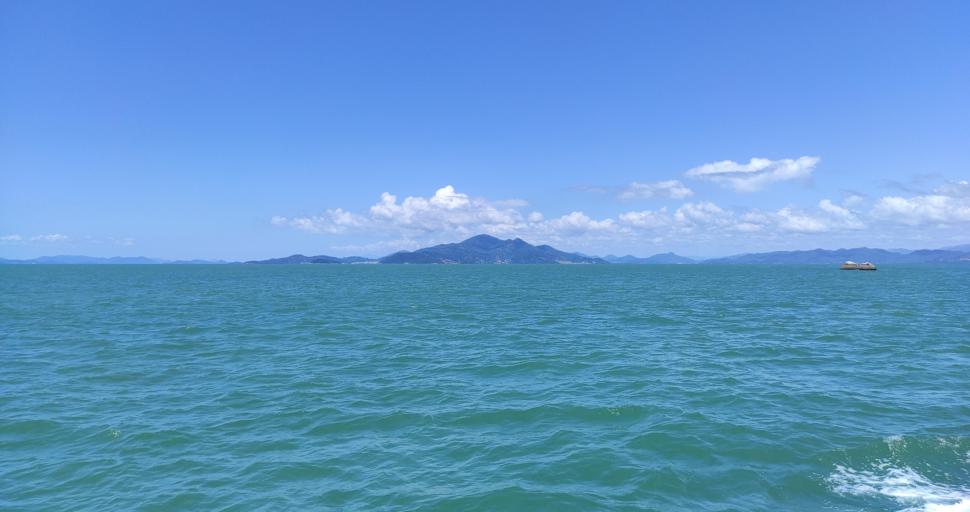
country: BR
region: Santa Catarina
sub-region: Porto Belo
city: Porto Belo
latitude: -27.2217
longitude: -48.5104
